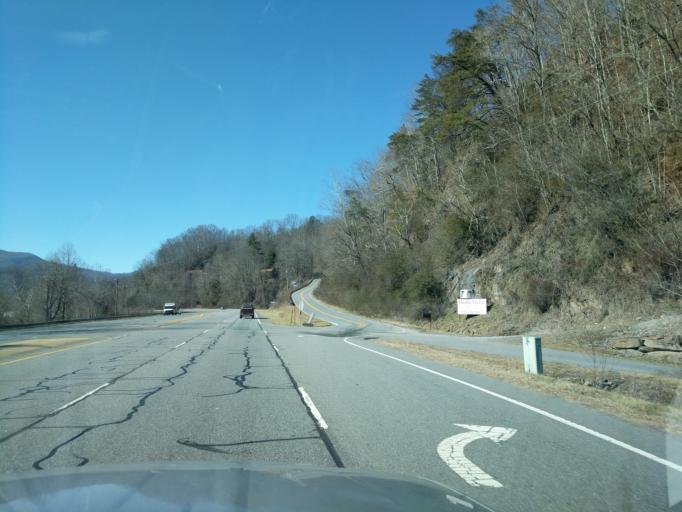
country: US
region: North Carolina
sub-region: Swain County
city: Cherokee
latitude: 35.4042
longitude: -83.3110
